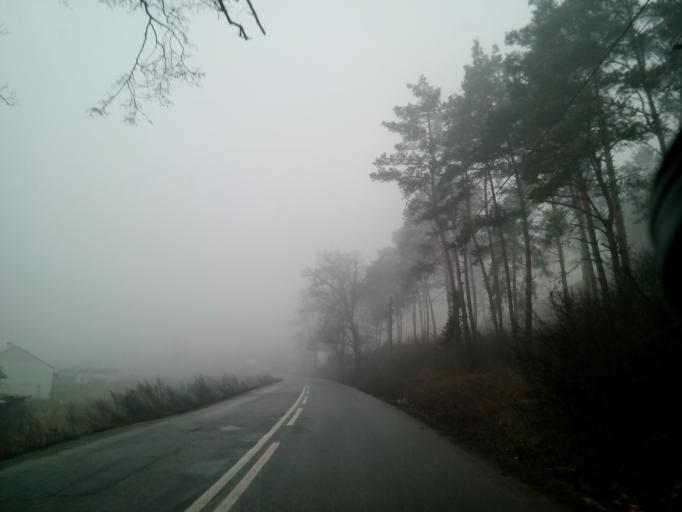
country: SK
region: Presovsky
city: Spisske Podhradie
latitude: 48.9731
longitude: 20.7817
